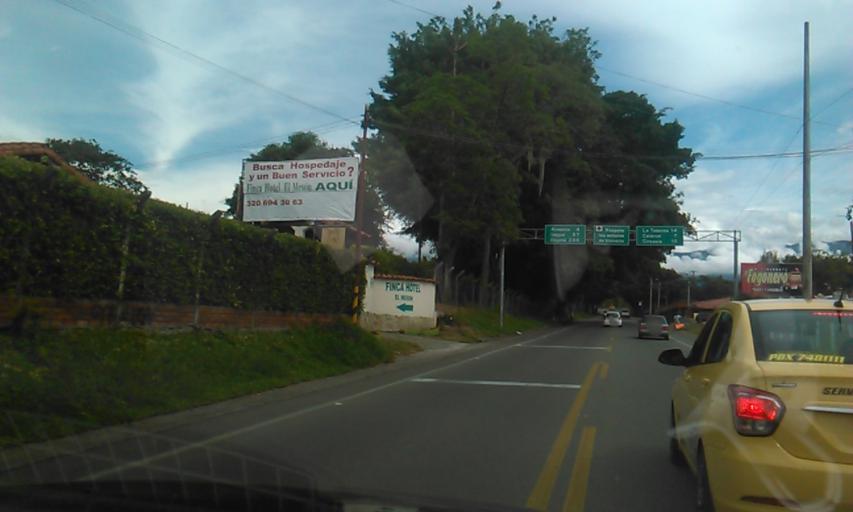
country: CO
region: Quindio
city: Armenia
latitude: 4.5297
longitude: -75.7246
